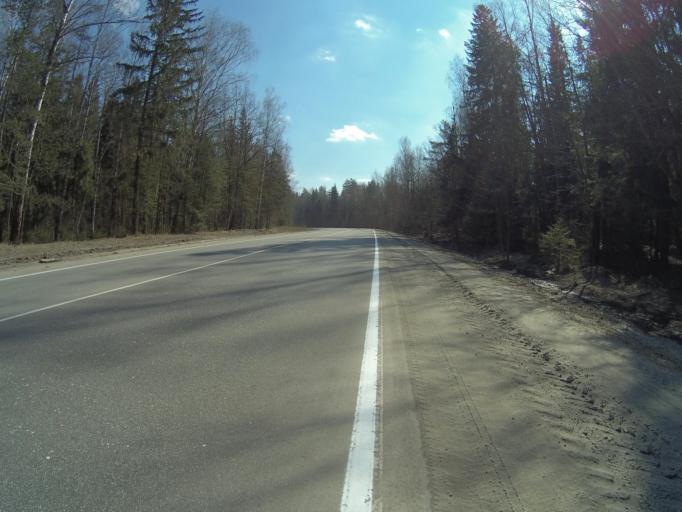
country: RU
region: Vladimir
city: Kommunar
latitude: 56.0228
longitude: 40.5742
